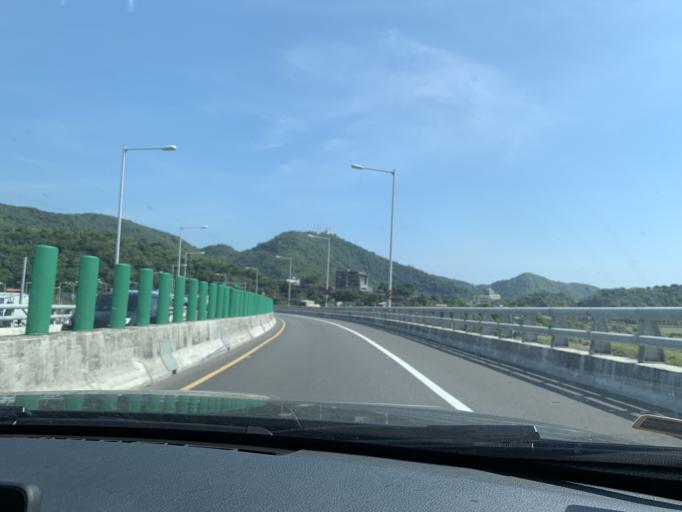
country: TW
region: Taiwan
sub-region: Yilan
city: Yilan
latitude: 24.5881
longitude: 121.8494
